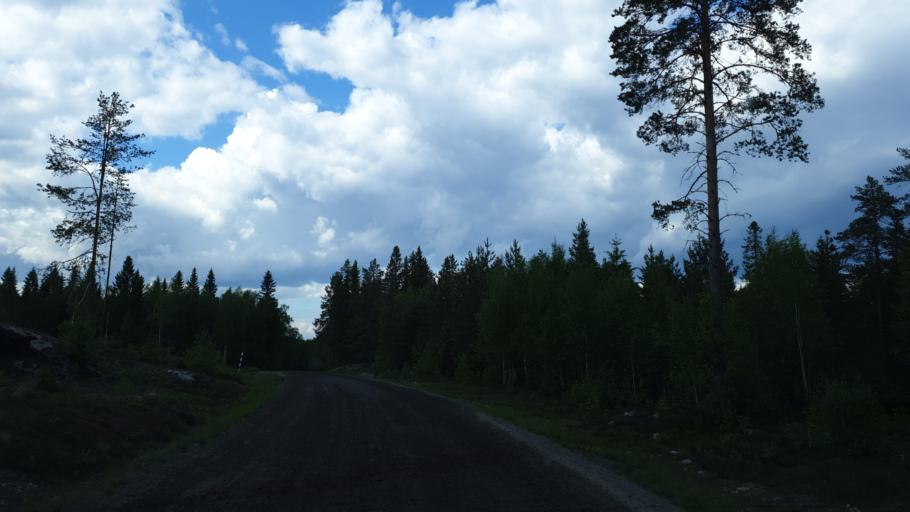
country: SE
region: Vaesterbotten
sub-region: Robertsfors Kommun
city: Robertsfors
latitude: 64.0325
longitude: 20.8853
